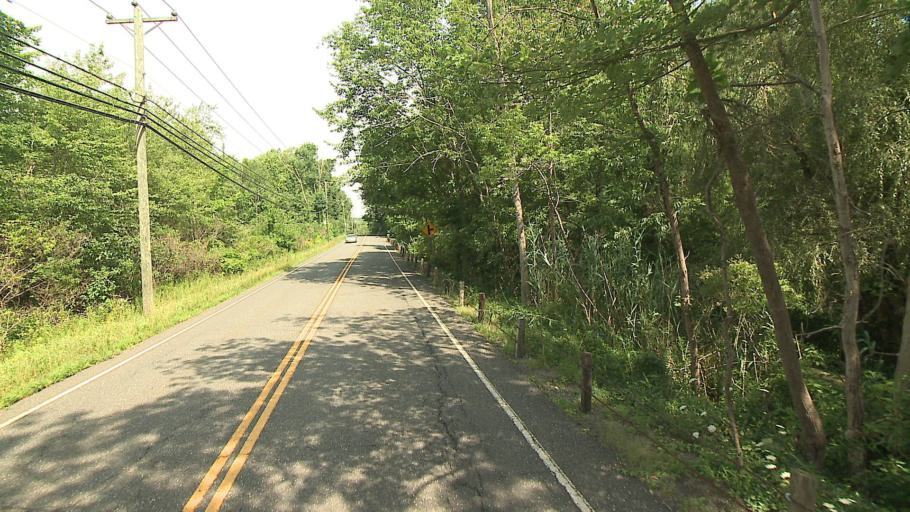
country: US
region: Connecticut
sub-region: Fairfield County
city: Sherman
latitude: 41.5700
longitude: -73.4979
